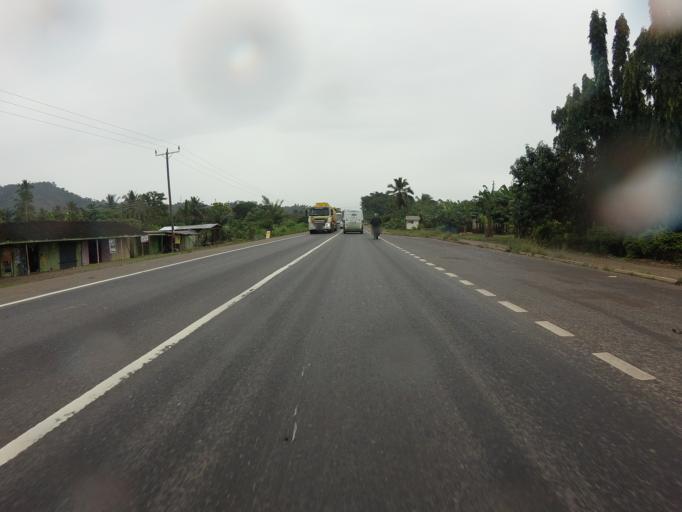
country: GH
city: Kibi
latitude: 6.1308
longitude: -0.4949
